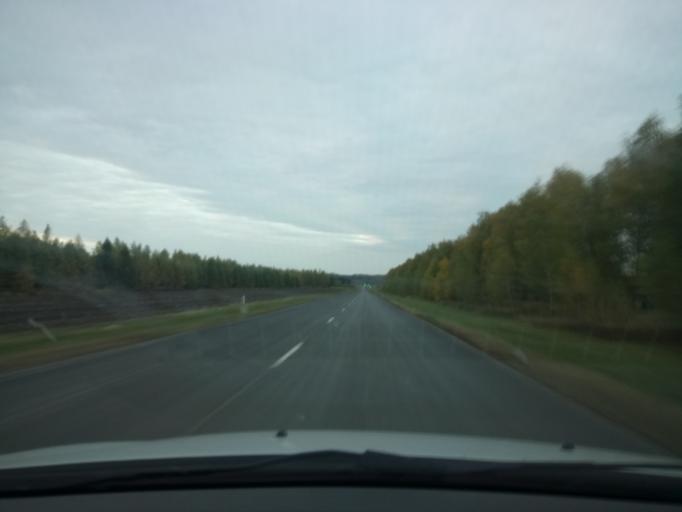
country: RU
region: Nizjnij Novgorod
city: Bol'shoye Murashkino
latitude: 55.7838
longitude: 44.7424
